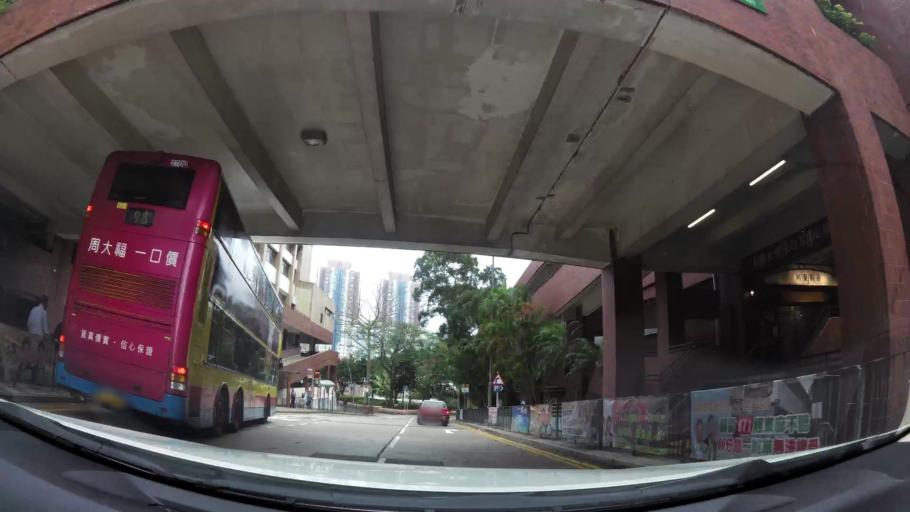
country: HK
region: Central and Western
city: Central
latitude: 22.2413
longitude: 114.1548
